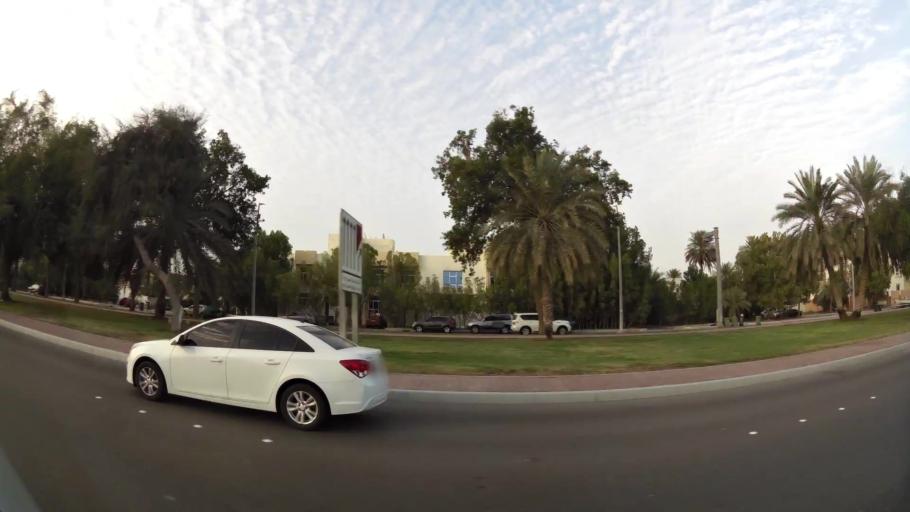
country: AE
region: Abu Dhabi
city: Abu Dhabi
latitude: 24.4283
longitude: 54.3970
